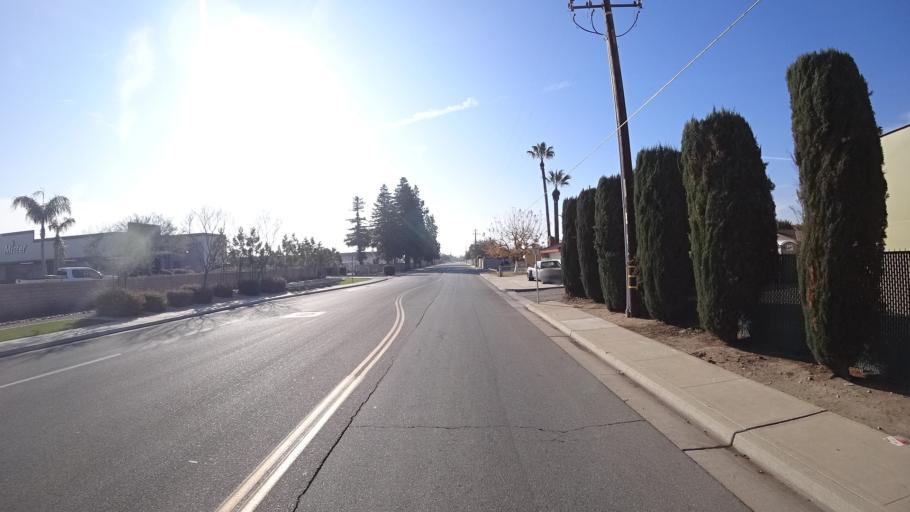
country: US
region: California
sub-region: Kern County
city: Oildale
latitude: 35.4119
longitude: -119.0622
